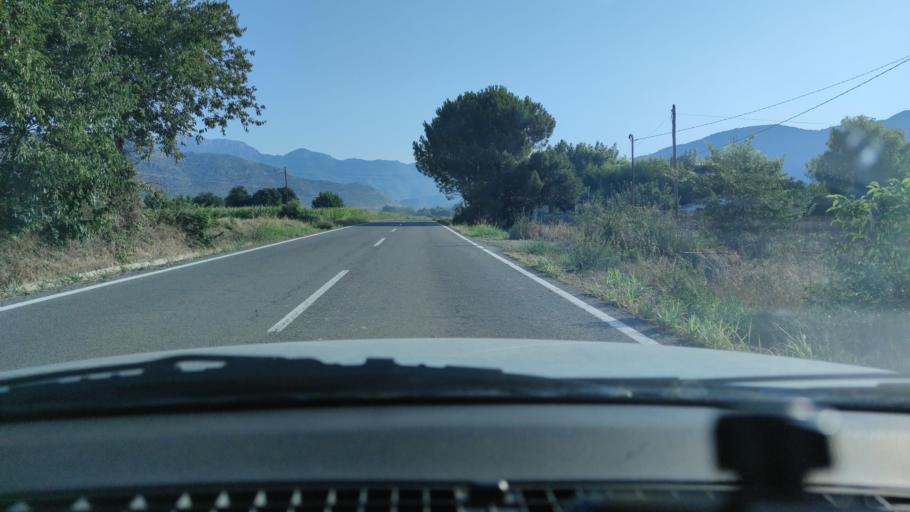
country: ES
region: Catalonia
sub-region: Provincia de Lleida
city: Camarasa
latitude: 41.8496
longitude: 0.8266
